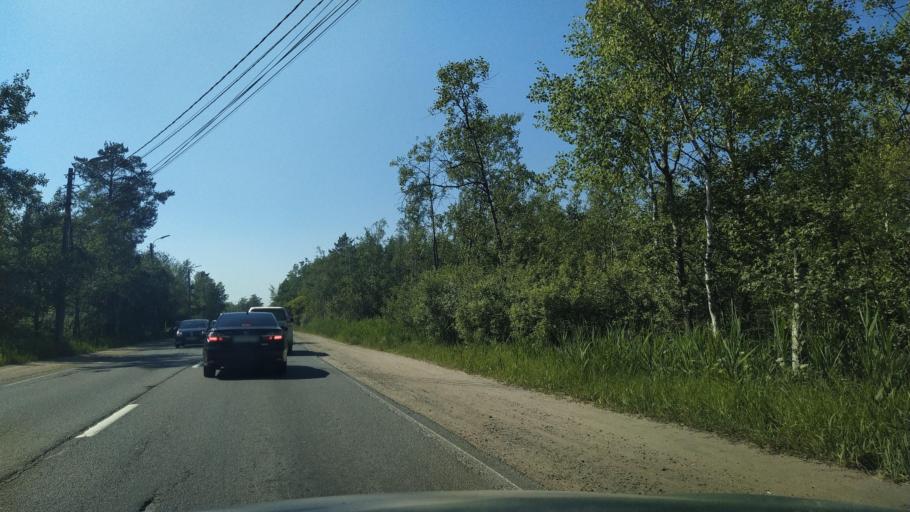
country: RU
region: St.-Petersburg
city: Beloostrov
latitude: 60.1427
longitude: 30.0151
